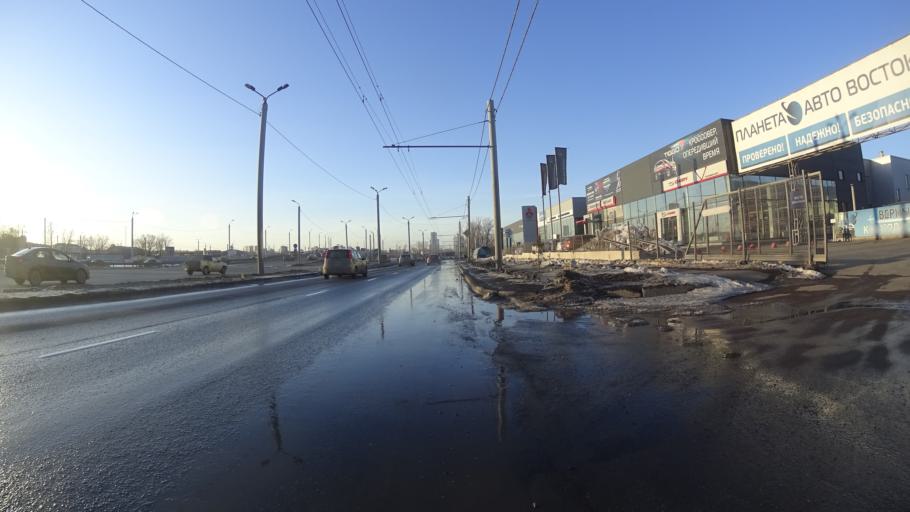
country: RU
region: Chelyabinsk
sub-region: Gorod Chelyabinsk
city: Chelyabinsk
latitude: 55.1485
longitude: 61.4458
